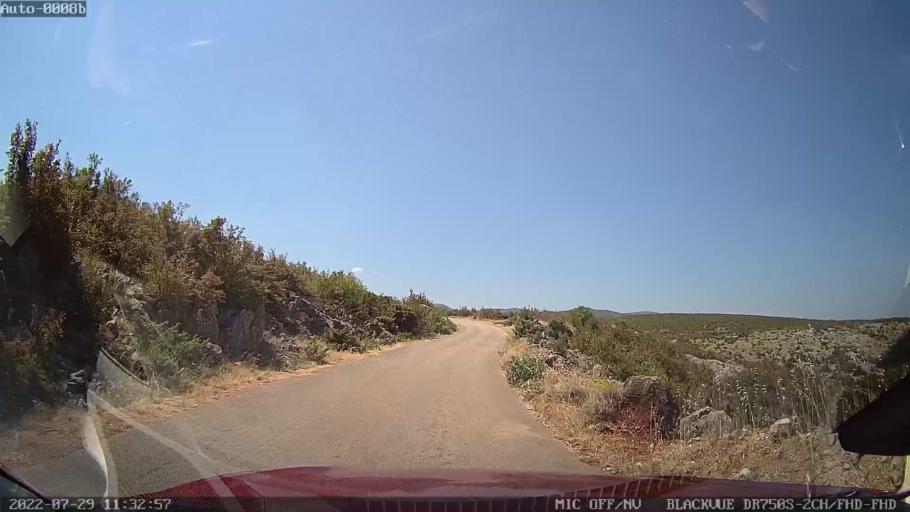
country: HR
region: Zadarska
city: Obrovac
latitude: 44.1899
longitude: 15.7334
